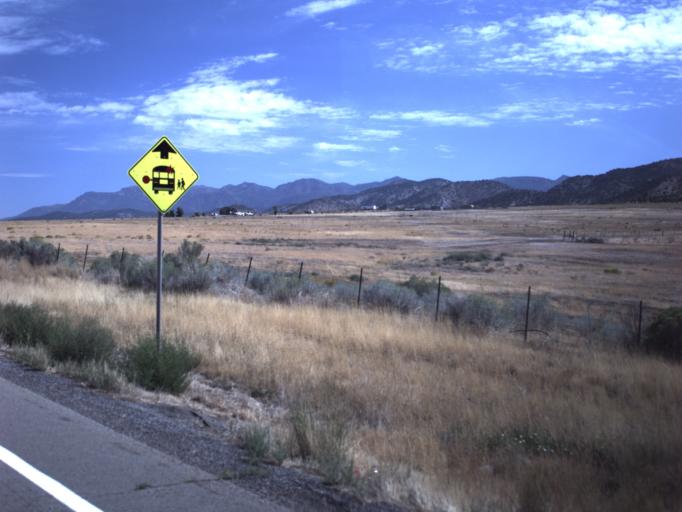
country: US
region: Utah
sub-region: Juab County
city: Nephi
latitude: 39.5323
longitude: -111.8639
